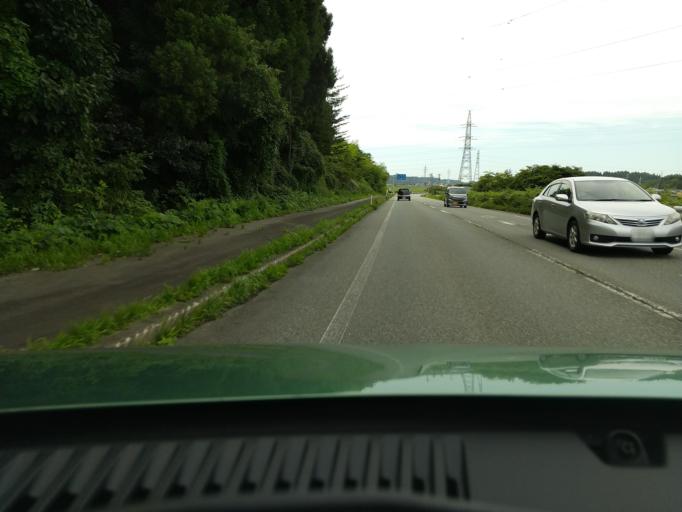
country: JP
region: Akita
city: Akita Shi
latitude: 39.8140
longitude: 140.0893
